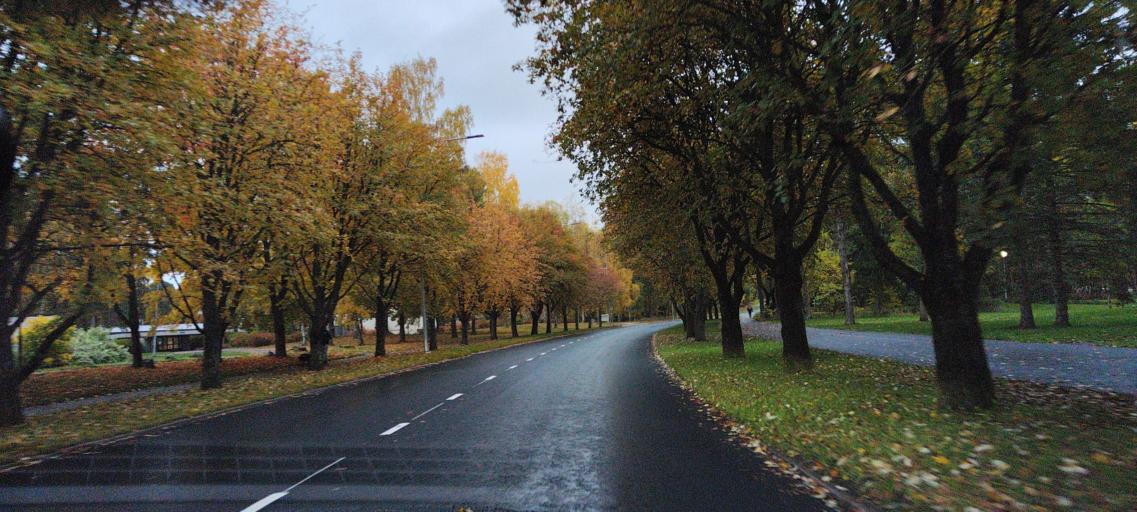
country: FI
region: Varsinais-Suomi
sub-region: Turku
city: Turku
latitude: 60.4321
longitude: 22.2922
